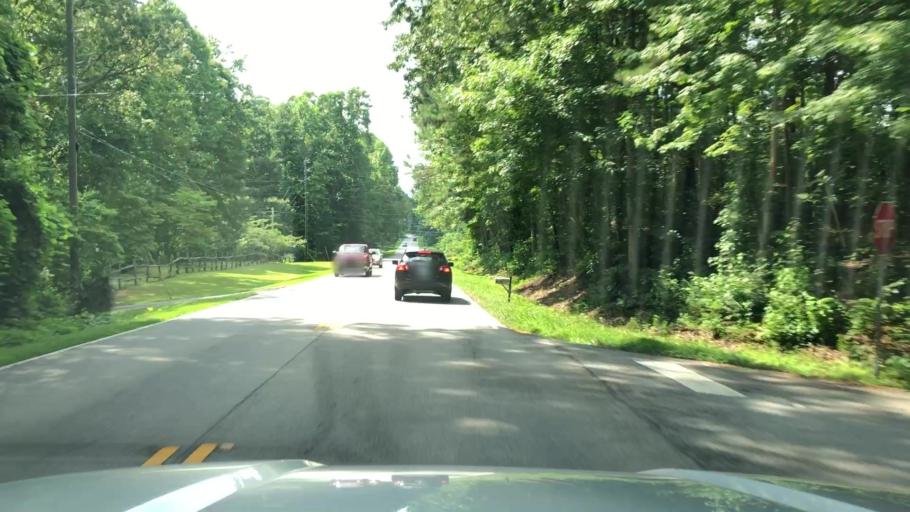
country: US
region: Georgia
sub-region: Paulding County
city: Dallas
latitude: 33.9489
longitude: -84.7725
